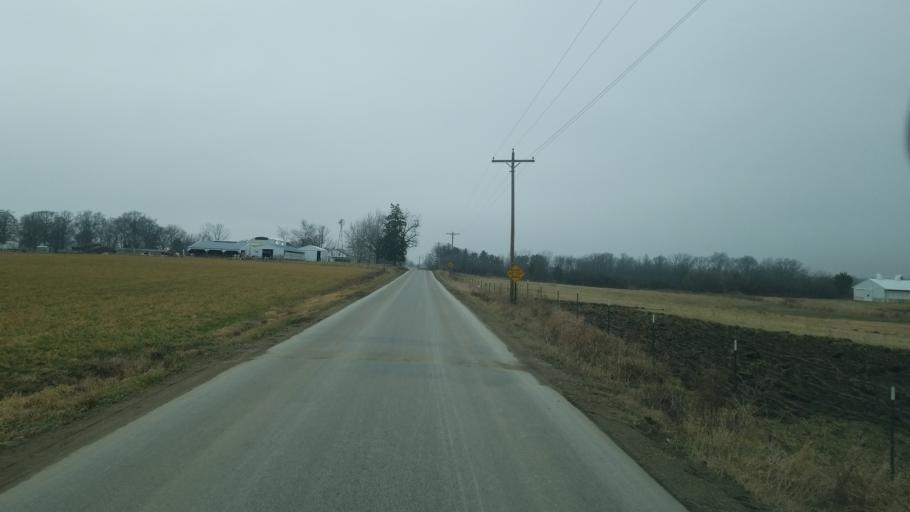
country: US
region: Indiana
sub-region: Adams County
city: Geneva
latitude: 40.6150
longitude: -84.9139
